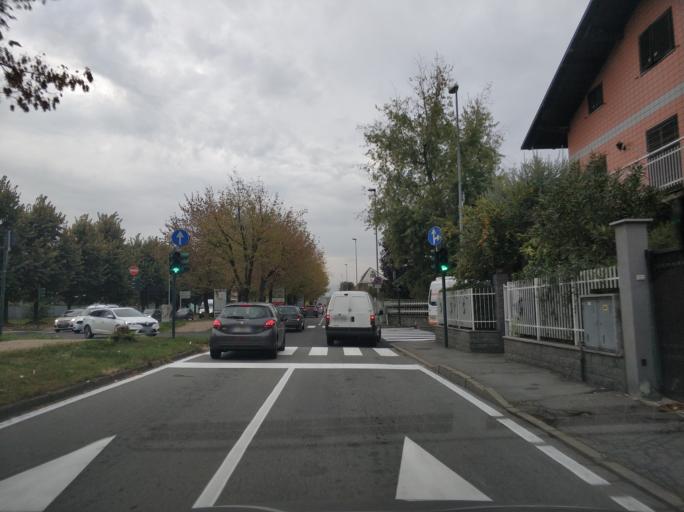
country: IT
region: Piedmont
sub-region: Provincia di Torino
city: Settimo Torinese
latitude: 45.1404
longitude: 7.7570
